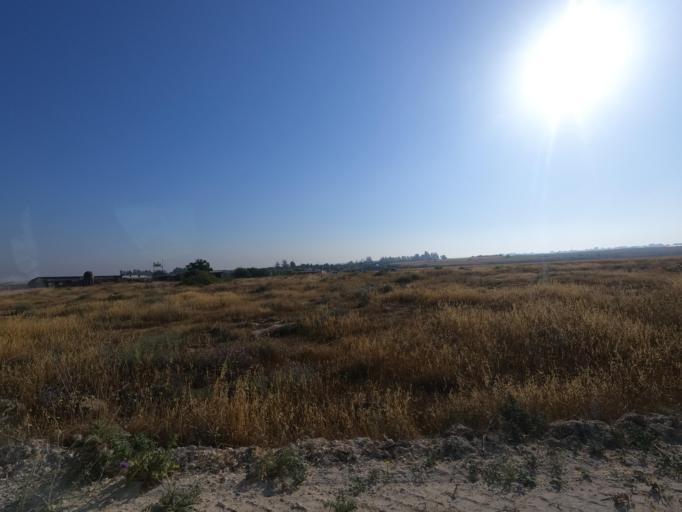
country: CY
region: Ammochostos
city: Acheritou
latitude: 35.0989
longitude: 33.8833
